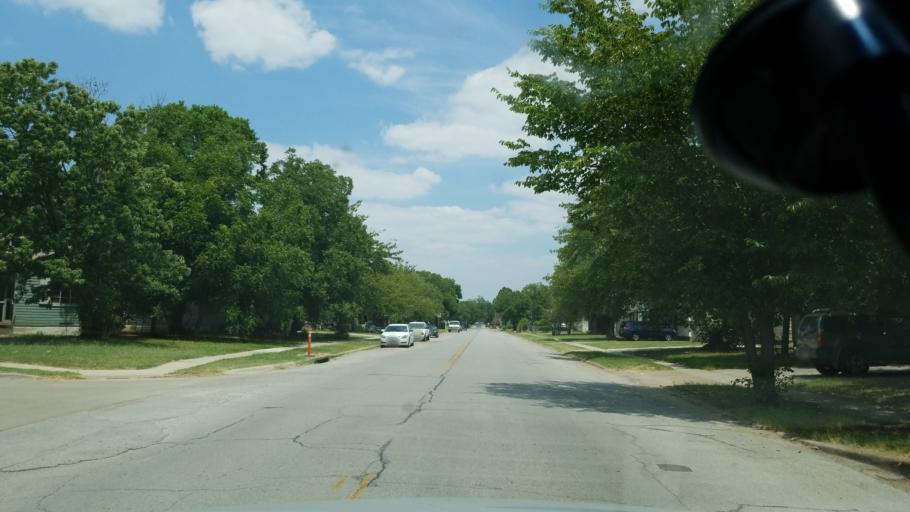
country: US
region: Texas
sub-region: Dallas County
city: Grand Prairie
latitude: 32.7512
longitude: -96.9780
